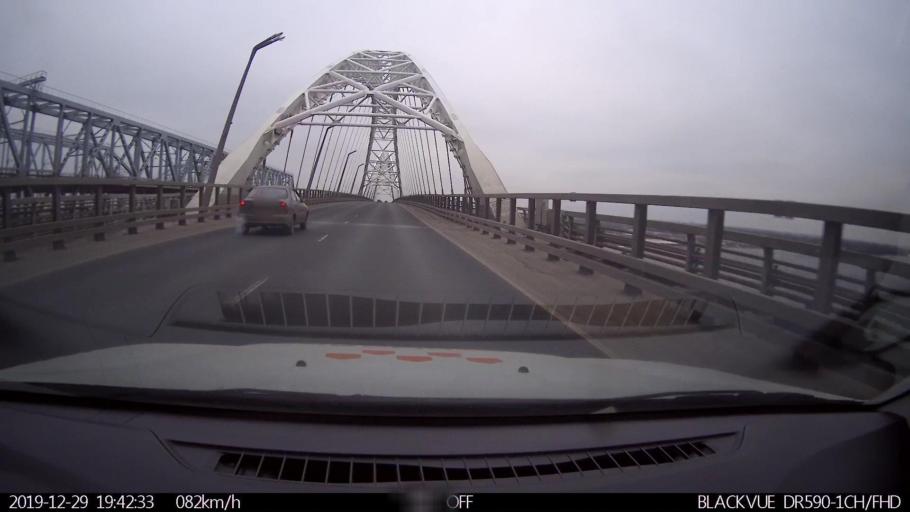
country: RU
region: Nizjnij Novgorod
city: Nizhniy Novgorod
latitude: 56.3518
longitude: 43.9233
